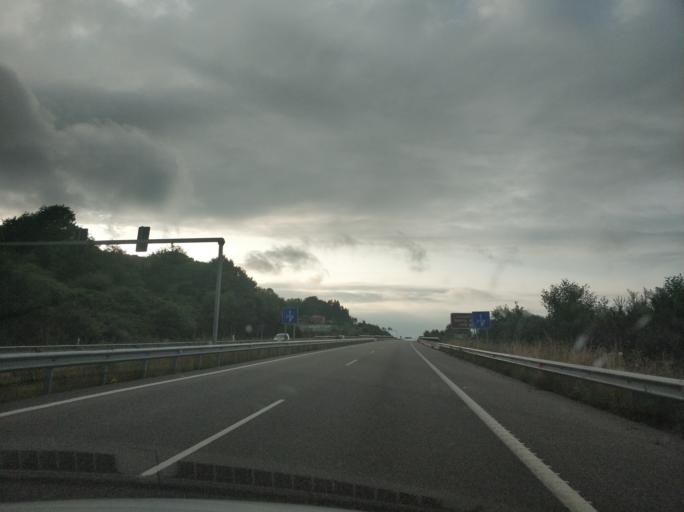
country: ES
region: Asturias
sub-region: Province of Asturias
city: Cudillero
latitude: 43.5484
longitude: -6.1626
